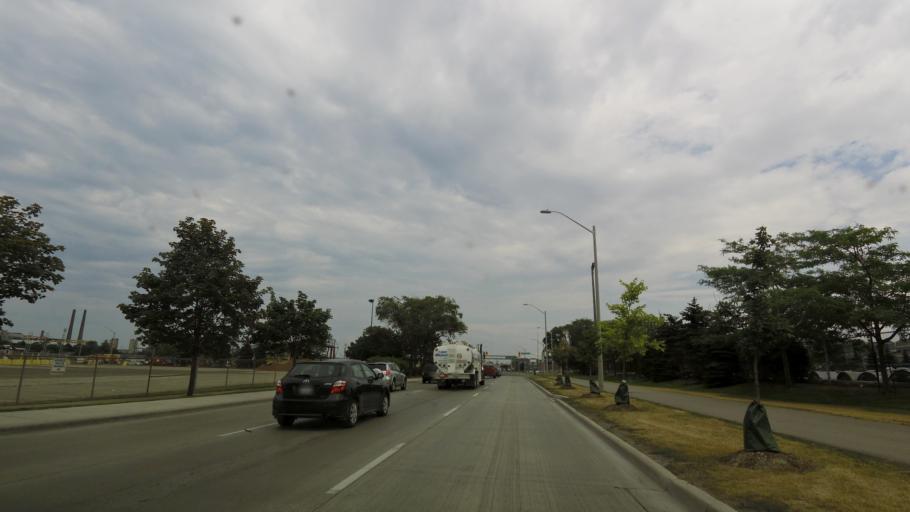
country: CA
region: Ontario
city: Hamilton
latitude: 43.2607
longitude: -79.8140
